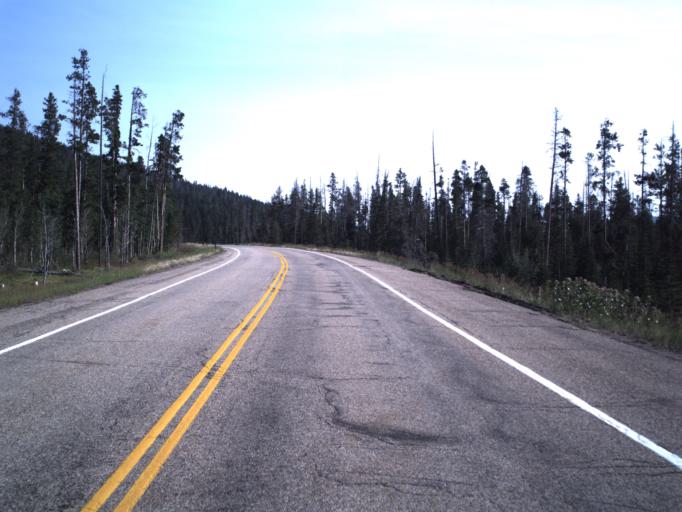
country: US
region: Utah
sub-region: Daggett County
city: Manila
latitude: 40.8150
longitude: -109.4663
